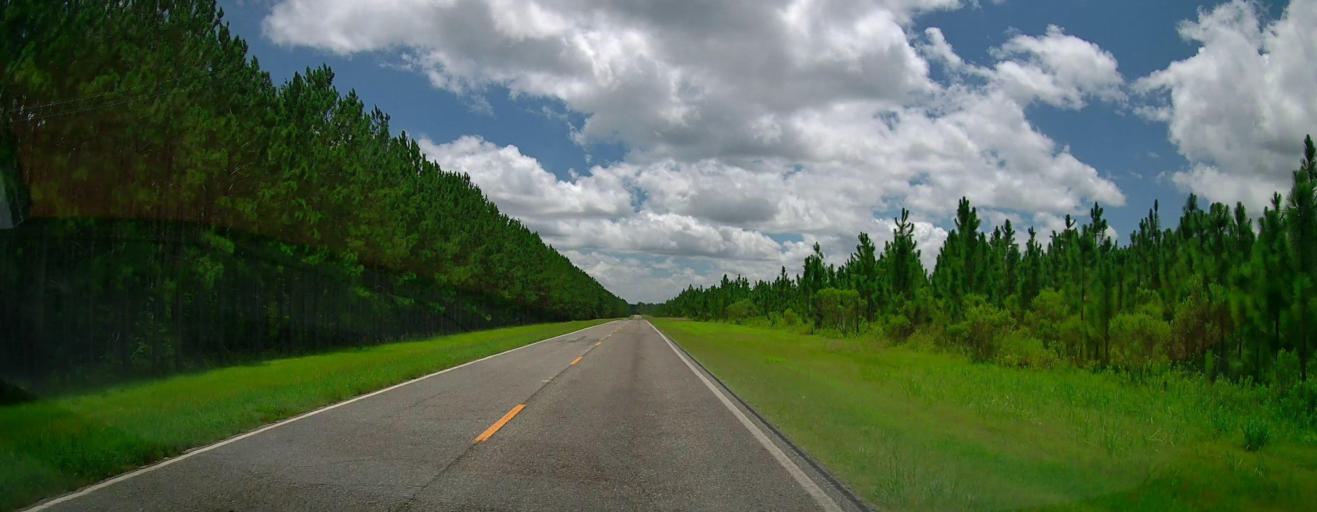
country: US
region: Georgia
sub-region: Wilcox County
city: Rochelle
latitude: 31.8705
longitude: -83.5584
